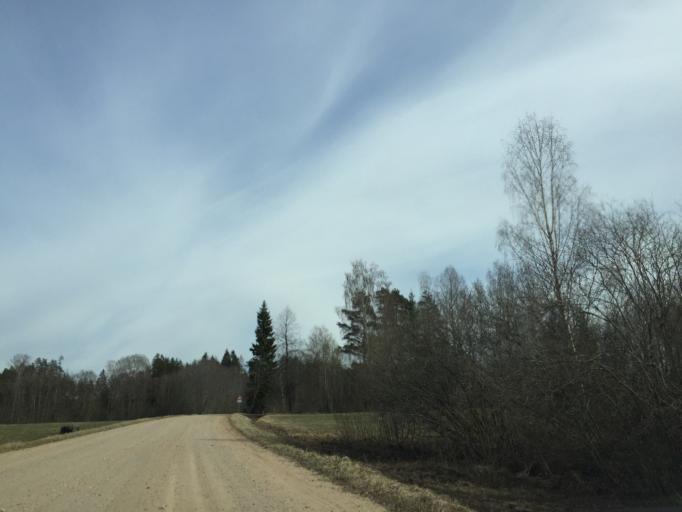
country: LV
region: Valkas Rajons
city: Valka
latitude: 57.8145
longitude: 25.8373
